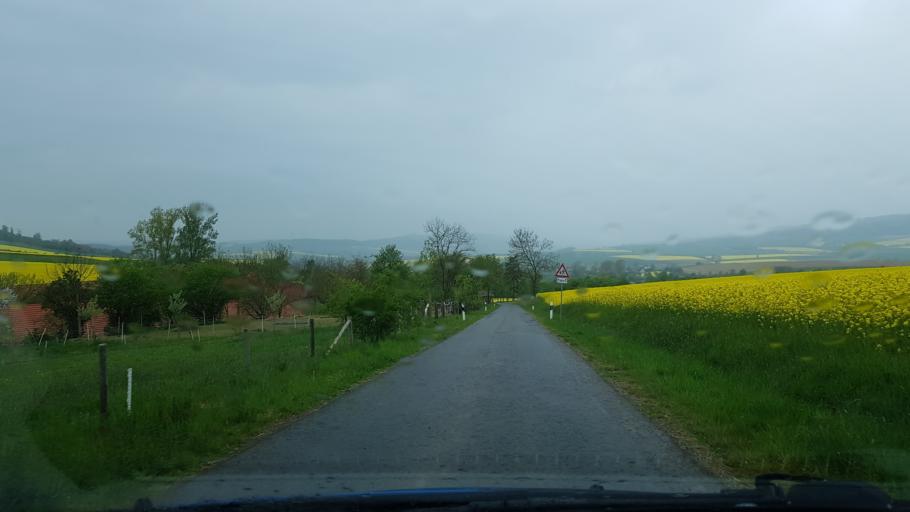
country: DE
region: Lower Saxony
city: Einbeck
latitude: 51.8615
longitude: 9.8864
